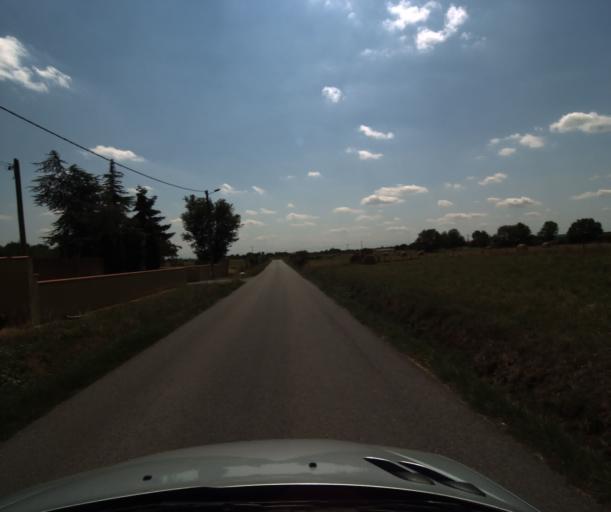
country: FR
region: Midi-Pyrenees
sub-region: Departement de la Haute-Garonne
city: Saint-Lys
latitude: 43.5083
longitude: 1.1859
